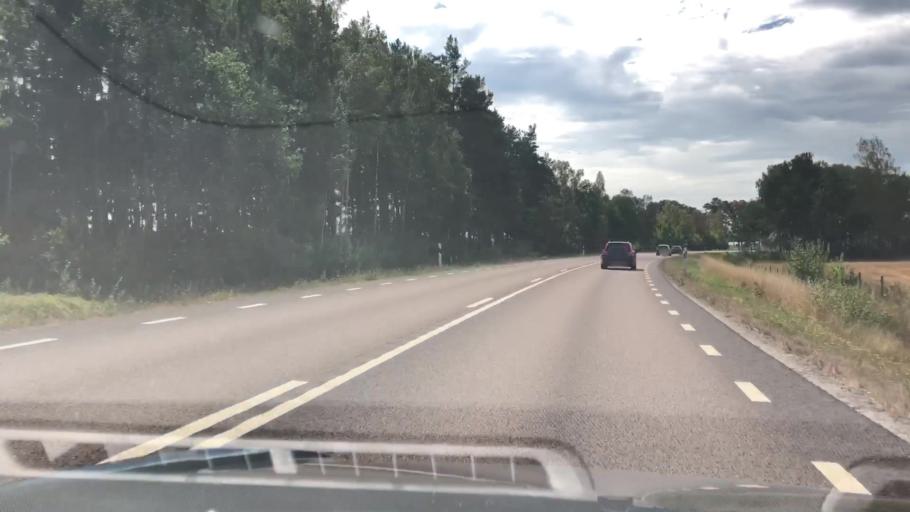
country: SE
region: Kalmar
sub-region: Torsas Kommun
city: Torsas
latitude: 56.3603
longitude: 16.0623
